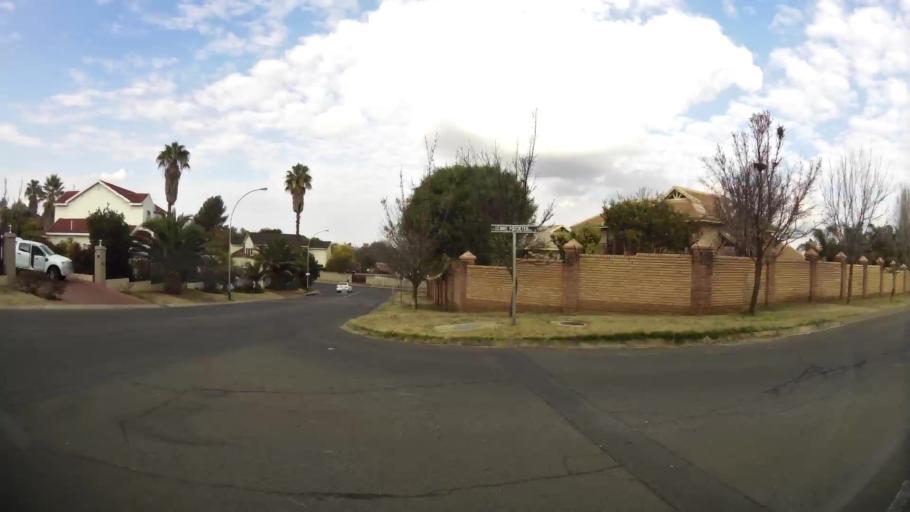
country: ZA
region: Orange Free State
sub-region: Mangaung Metropolitan Municipality
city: Bloemfontein
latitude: -29.0854
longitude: 26.2019
